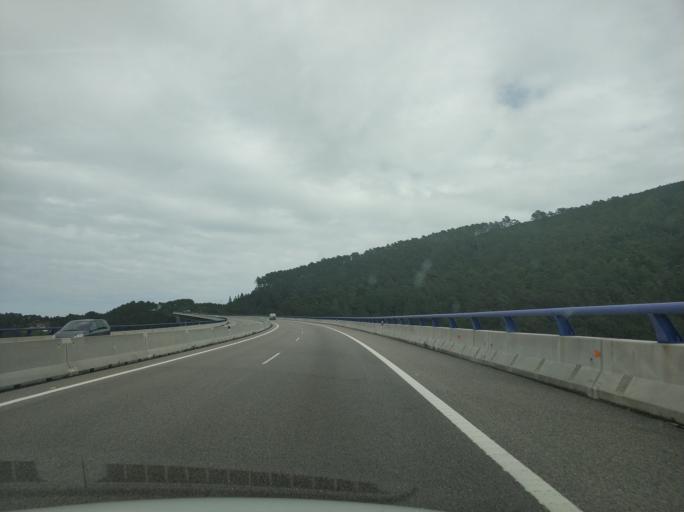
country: ES
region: Asturias
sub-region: Province of Asturias
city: Cudillero
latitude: 43.5552
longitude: -6.1912
